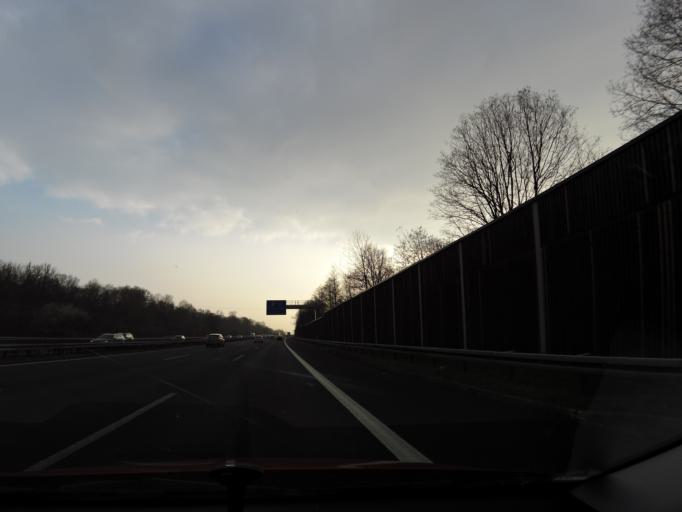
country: DE
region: Baden-Wuerttemberg
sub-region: Karlsruhe Region
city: Rastatt
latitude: 48.8329
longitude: 8.2205
